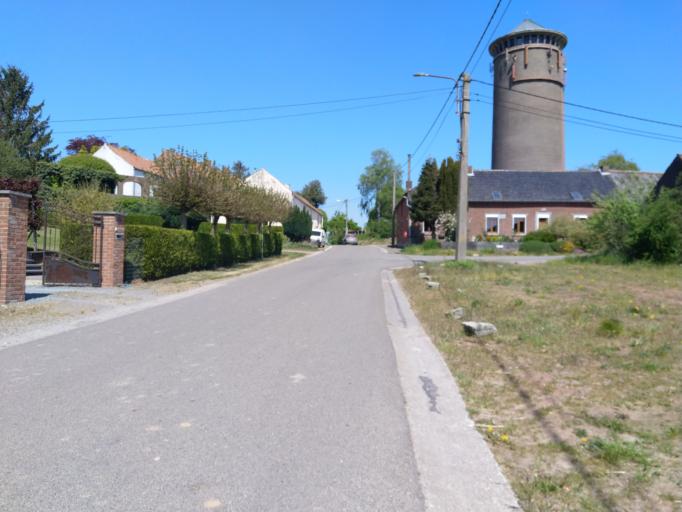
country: BE
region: Wallonia
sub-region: Province du Hainaut
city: Enghien
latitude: 50.6307
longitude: 4.0186
